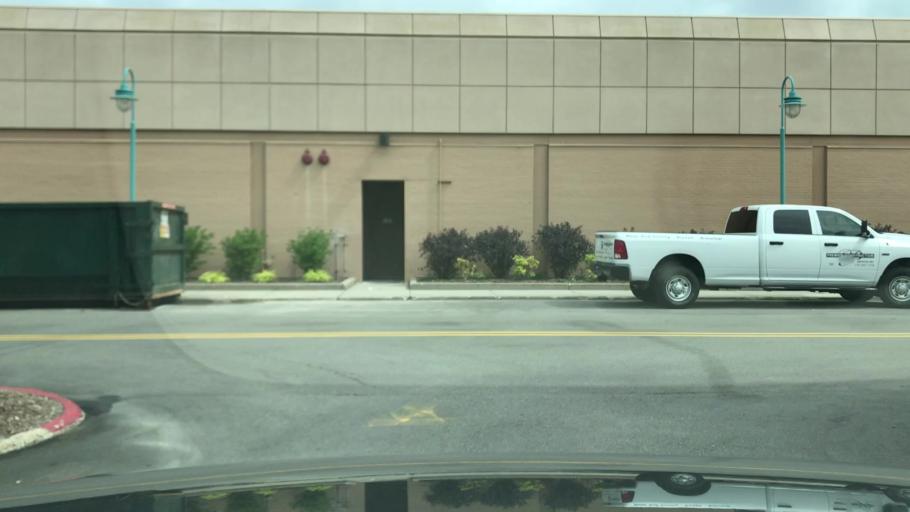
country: US
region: Michigan
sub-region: Kent County
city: East Grand Rapids
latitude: 42.9174
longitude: -85.5878
